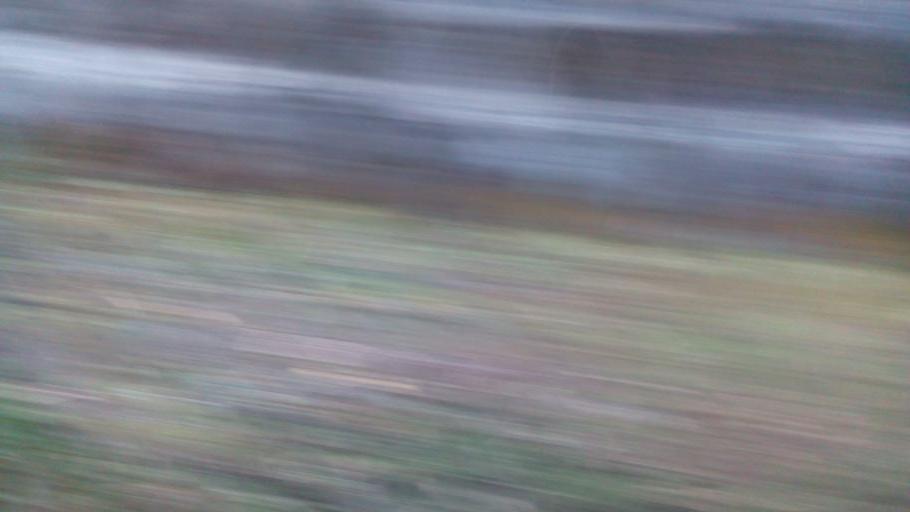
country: TW
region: Taiwan
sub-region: Yilan
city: Yilan
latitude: 24.5459
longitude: 121.4584
